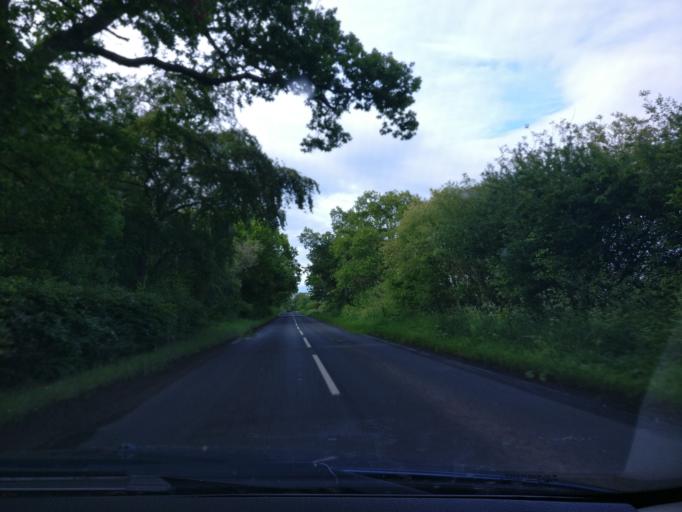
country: GB
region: Scotland
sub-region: East Lothian
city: Haddington
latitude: 55.9148
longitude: -2.7465
